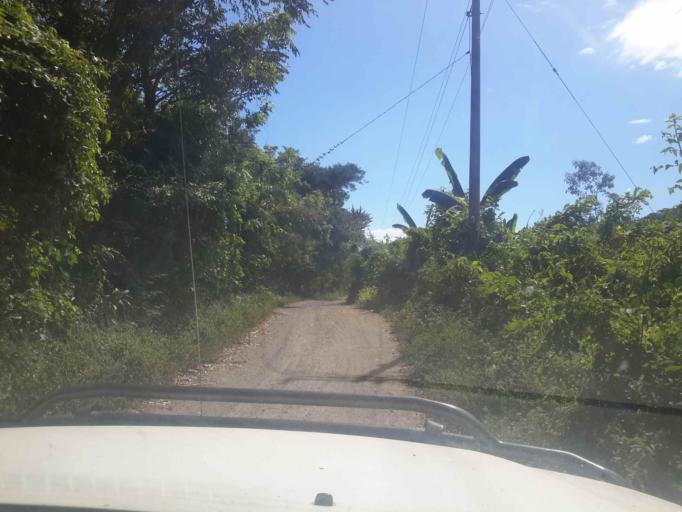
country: NI
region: Rivas
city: Altagracia
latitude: 11.4670
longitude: -85.4646
